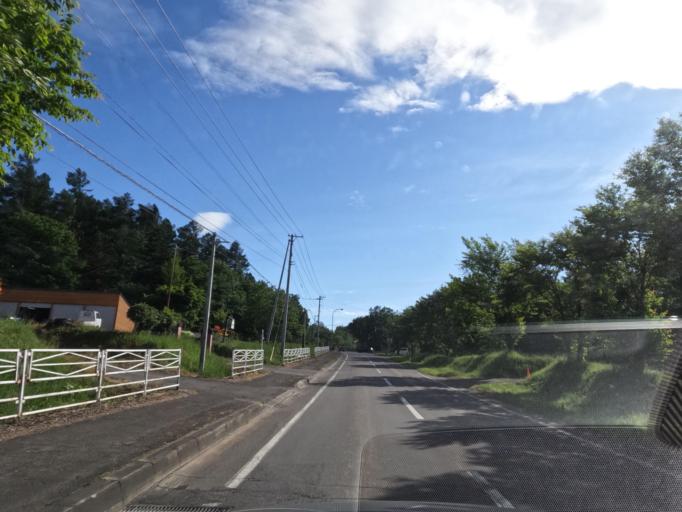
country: JP
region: Hokkaido
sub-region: Asahikawa-shi
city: Asahikawa
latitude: 43.6125
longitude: 142.4789
